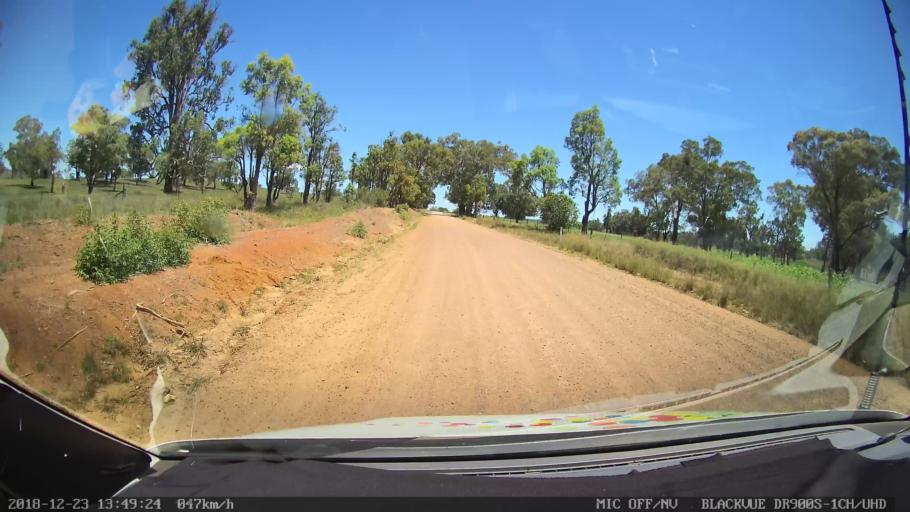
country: AU
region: New South Wales
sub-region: Tamworth Municipality
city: Manilla
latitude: -30.5211
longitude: 151.1085
